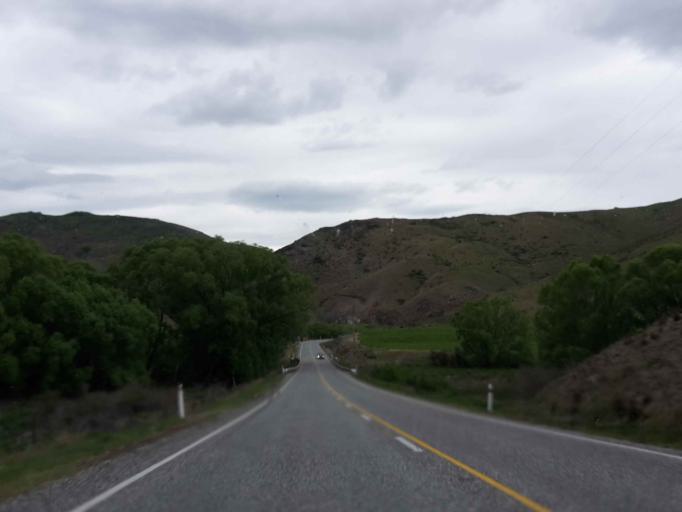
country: NZ
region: Otago
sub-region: Queenstown-Lakes District
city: Wanaka
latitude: -44.7027
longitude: 169.5008
